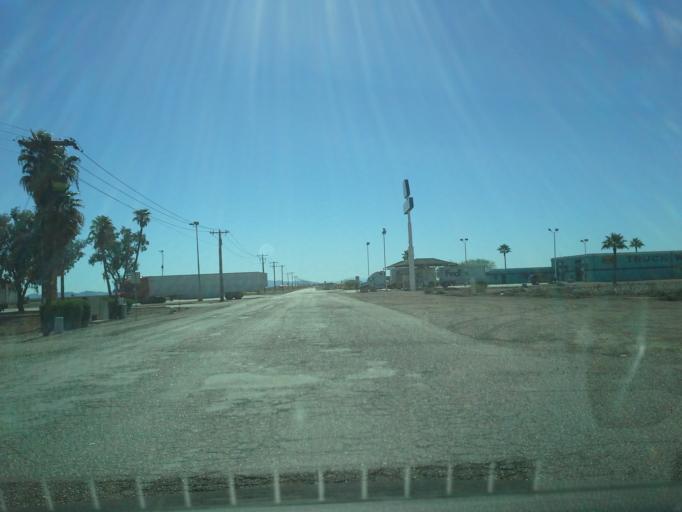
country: US
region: Arizona
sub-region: Pinal County
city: Eloy
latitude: 32.7326
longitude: -111.5504
